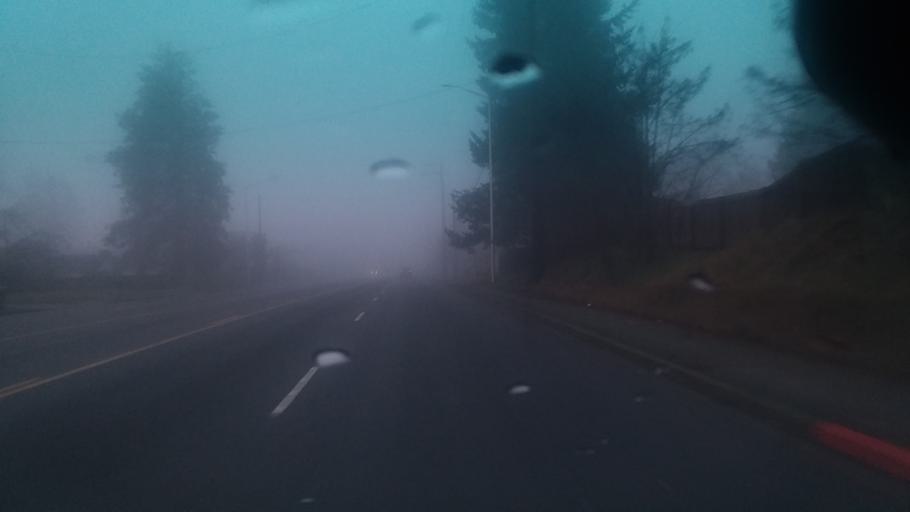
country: US
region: Washington
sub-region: Pierce County
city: Summit
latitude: 47.1549
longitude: -122.3312
